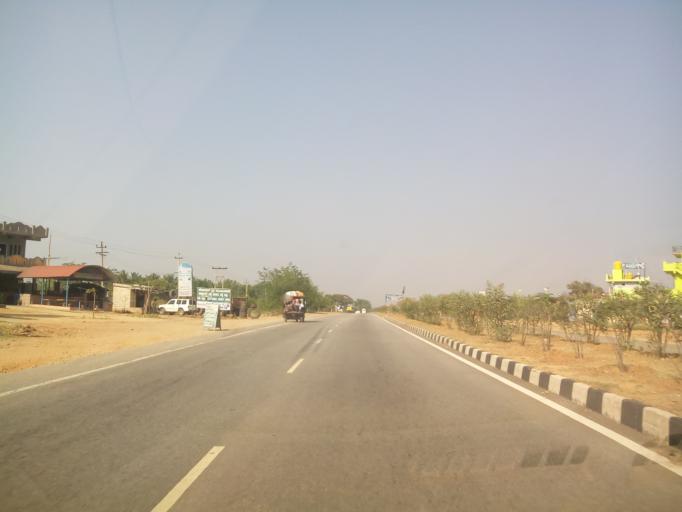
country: IN
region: Karnataka
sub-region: Tumkur
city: Kunigal
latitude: 13.0367
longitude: 77.0971
